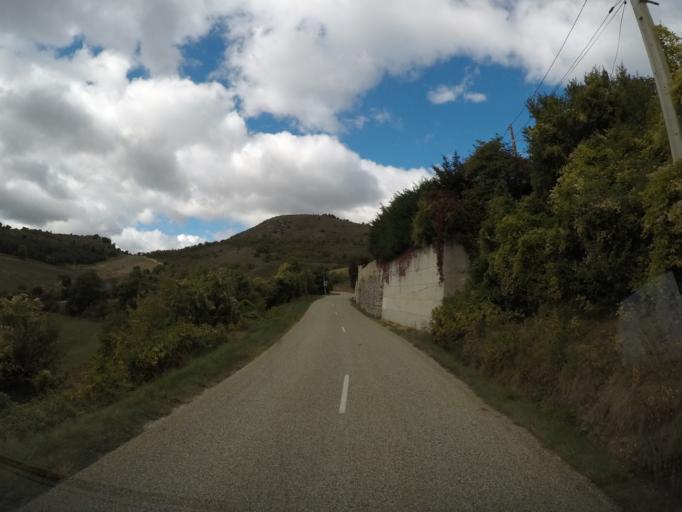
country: FR
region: Provence-Alpes-Cote d'Azur
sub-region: Departement du Vaucluse
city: Sault
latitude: 44.1855
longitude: 5.5139
